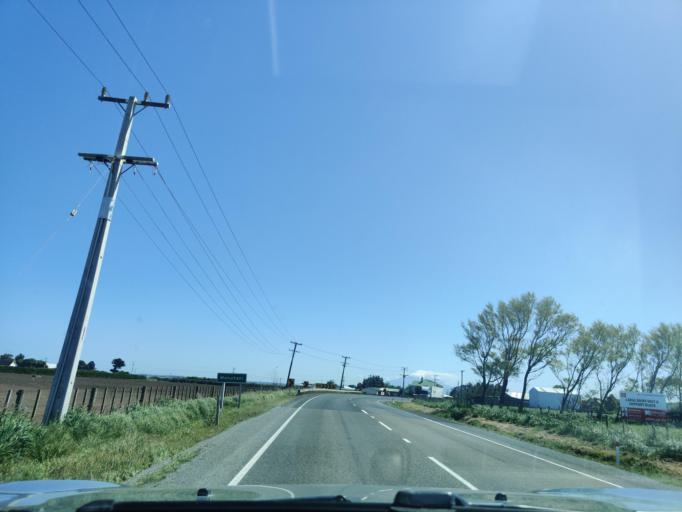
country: NZ
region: Taranaki
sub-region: South Taranaki District
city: Patea
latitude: -39.6624
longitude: 174.3980
